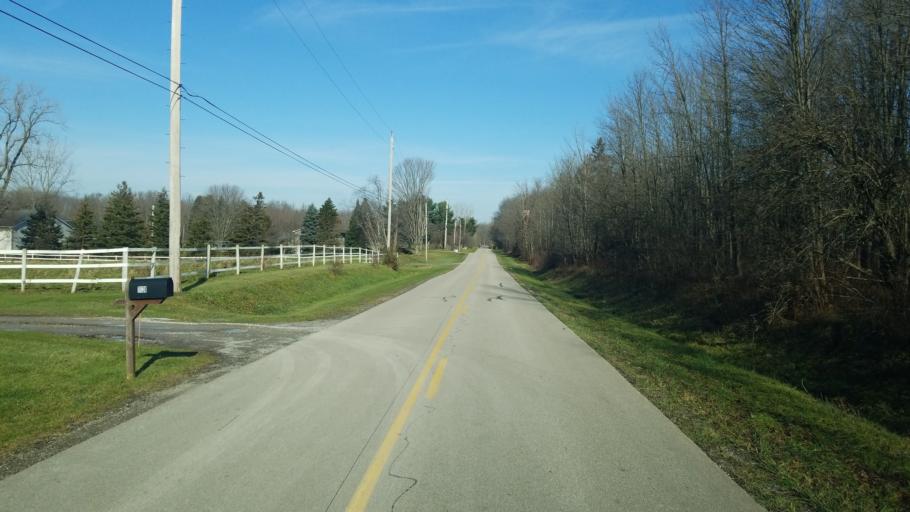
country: US
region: Ohio
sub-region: Ashtabula County
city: Jefferson
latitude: 41.7554
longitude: -80.7898
